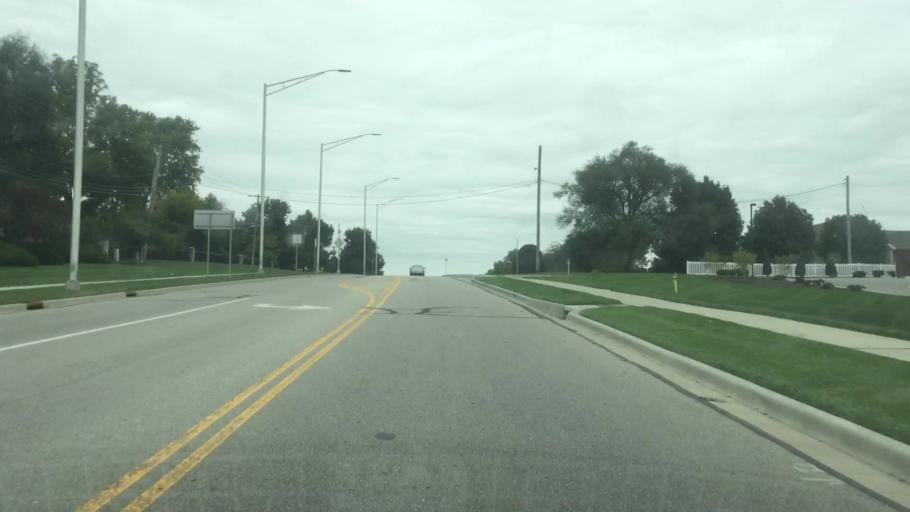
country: US
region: Kansas
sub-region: Johnson County
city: Lenexa
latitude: 38.9776
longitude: -94.7796
